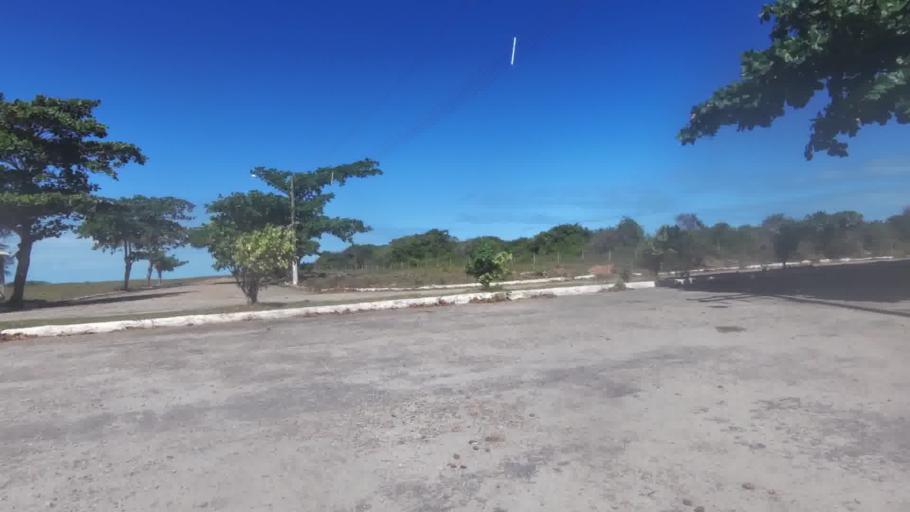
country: BR
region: Espirito Santo
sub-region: Marataizes
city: Marataizes
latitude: -21.1973
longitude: -40.9349
